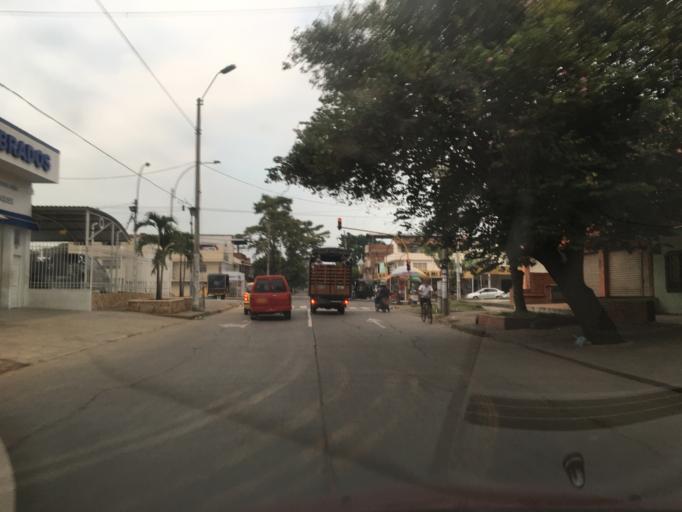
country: CO
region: Valle del Cauca
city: Cali
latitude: 3.4122
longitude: -76.5228
